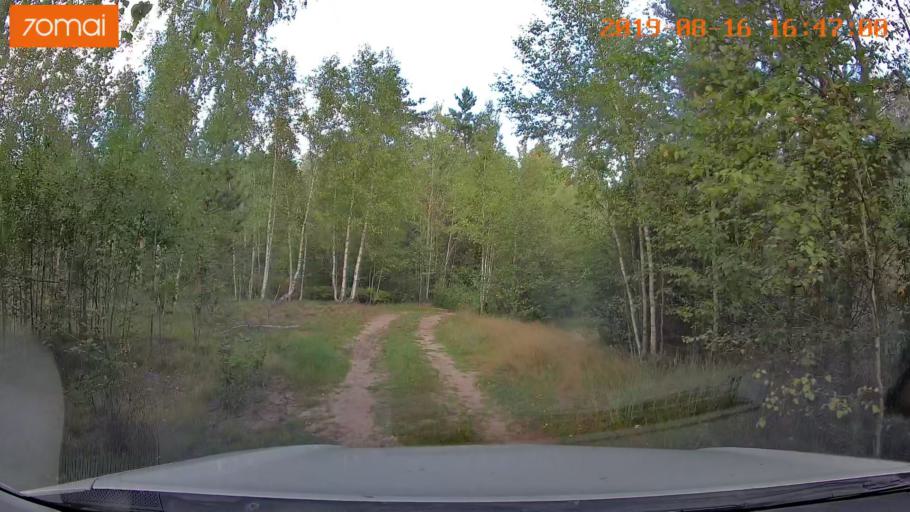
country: BY
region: Mogilev
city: Asipovichy
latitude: 53.2498
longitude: 28.7885
